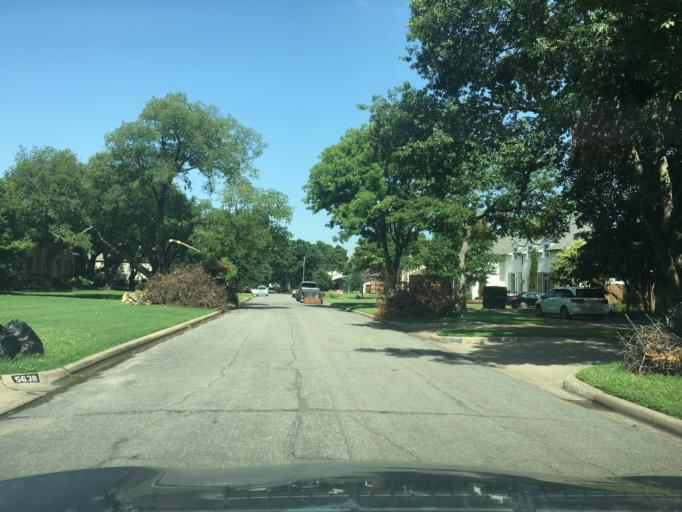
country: US
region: Texas
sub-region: Dallas County
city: University Park
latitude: 32.9045
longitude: -96.8096
